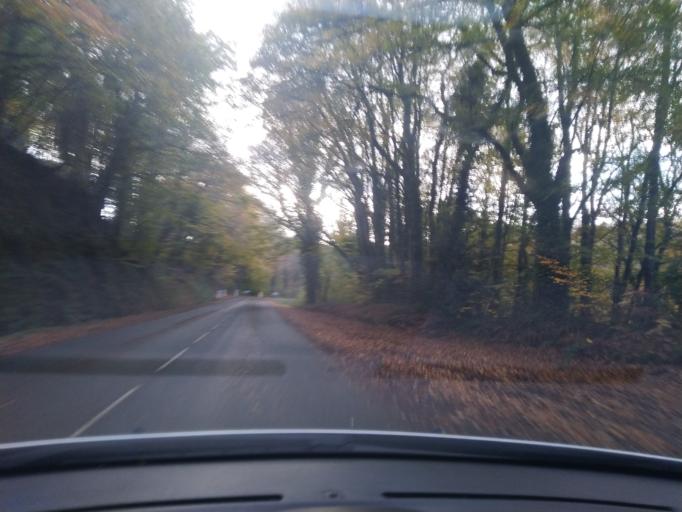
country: FR
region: Brittany
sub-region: Departement du Finistere
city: Plouigneau
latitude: 48.5705
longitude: -3.6442
